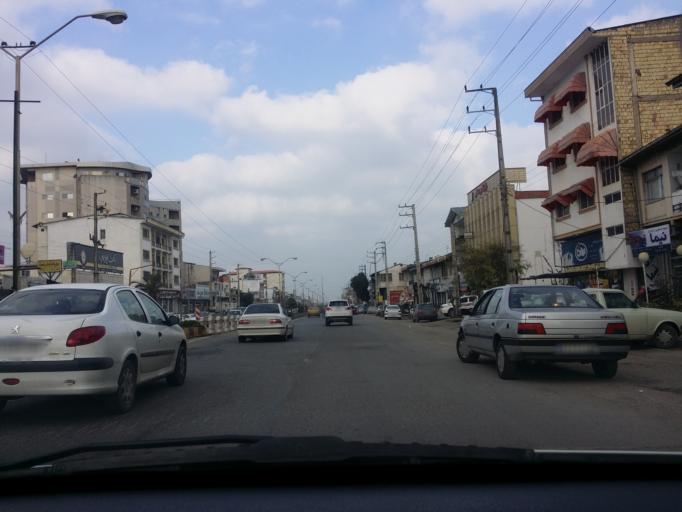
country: IR
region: Mazandaran
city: Chalus
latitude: 36.6665
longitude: 51.4100
